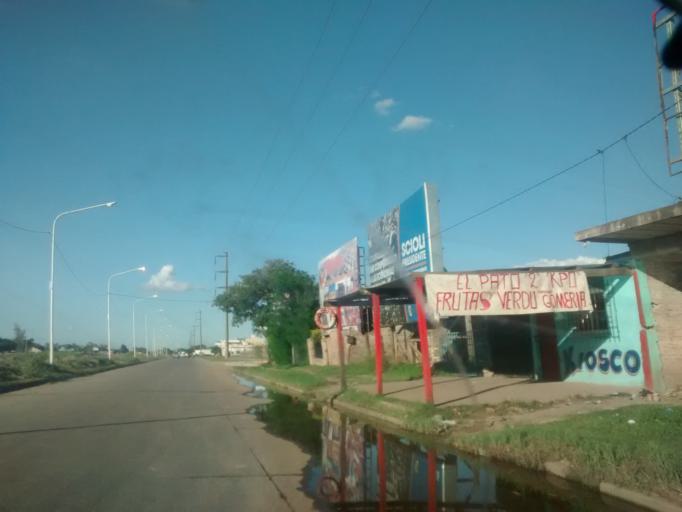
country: AR
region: Chaco
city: Fontana
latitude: -27.4474
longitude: -59.0241
